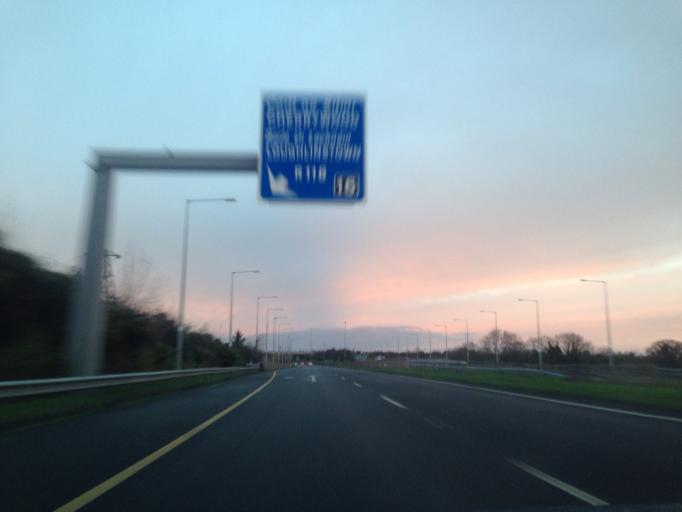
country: IE
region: Leinster
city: Loughlinstown
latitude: 53.2378
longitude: -6.1439
